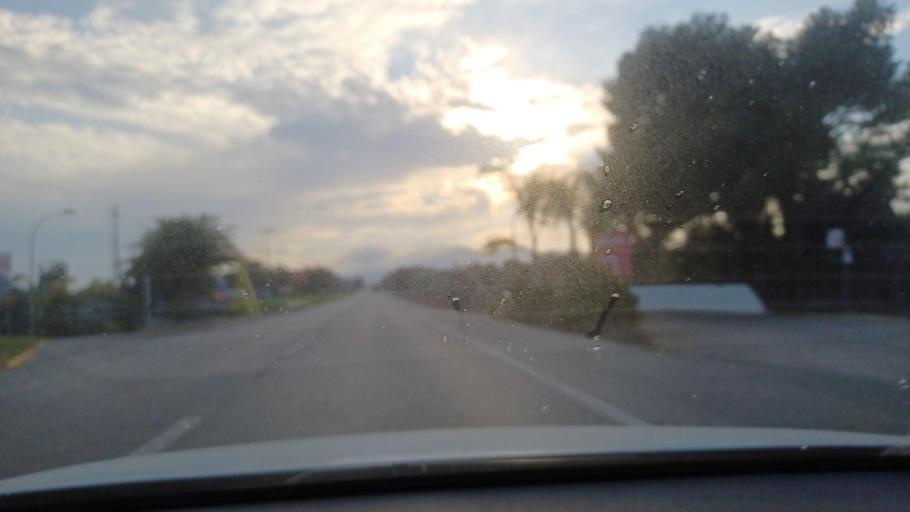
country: ES
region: Catalonia
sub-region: Provincia de Tarragona
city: Cambrils
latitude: 41.0419
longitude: 0.9824
